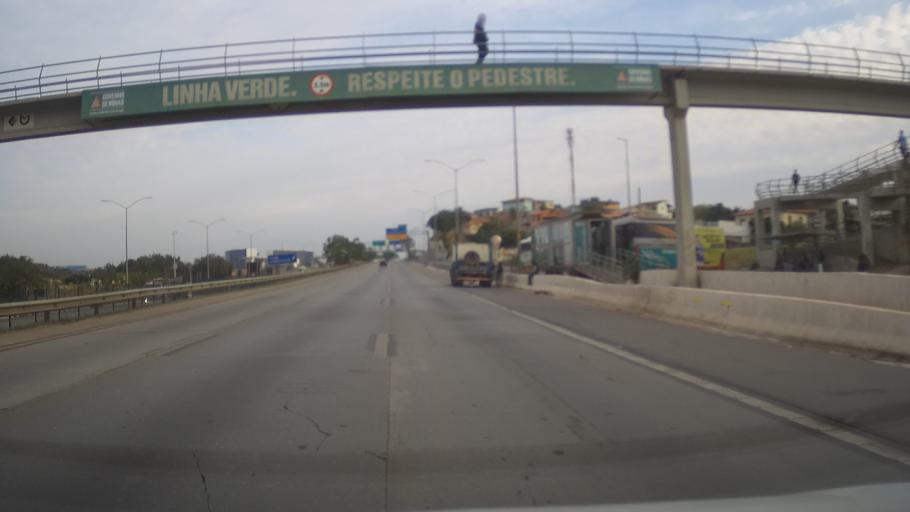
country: BR
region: Minas Gerais
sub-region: Santa Luzia
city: Santa Luzia
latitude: -19.7986
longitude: -43.9499
